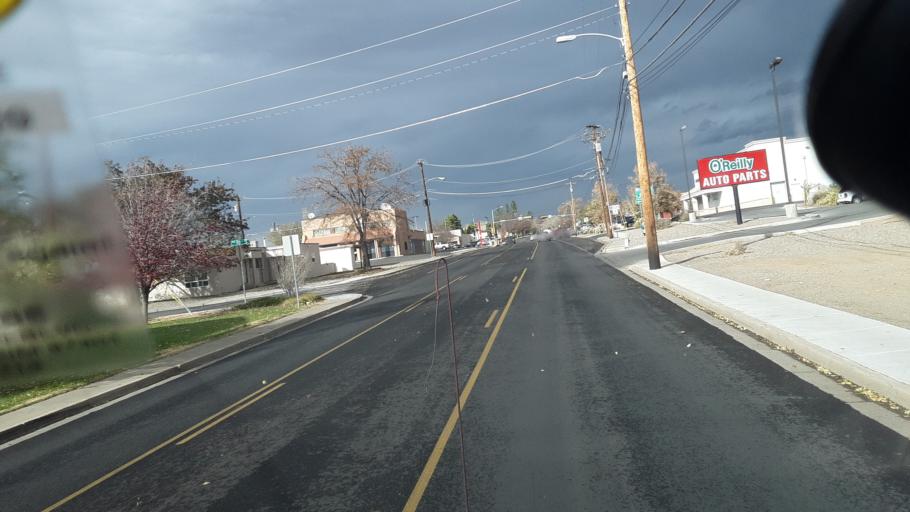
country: US
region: New Mexico
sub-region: San Juan County
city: Farmington
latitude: 36.7466
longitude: -108.1977
